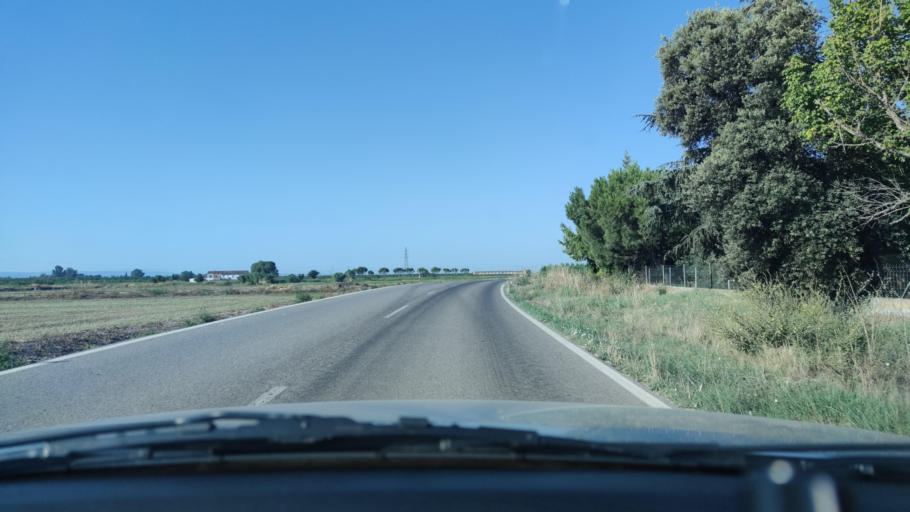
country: ES
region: Catalonia
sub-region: Provincia de Lleida
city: Bellvis
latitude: 41.6572
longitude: 0.8068
